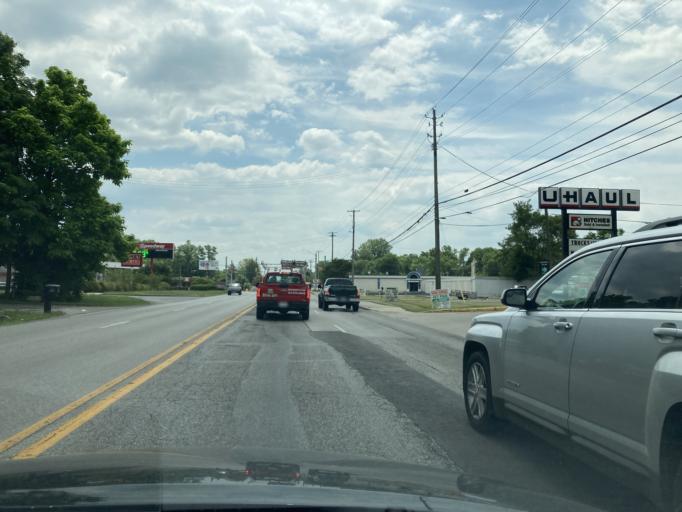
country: US
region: Indiana
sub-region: Marion County
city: Meridian Hills
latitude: 39.8632
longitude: -86.1994
